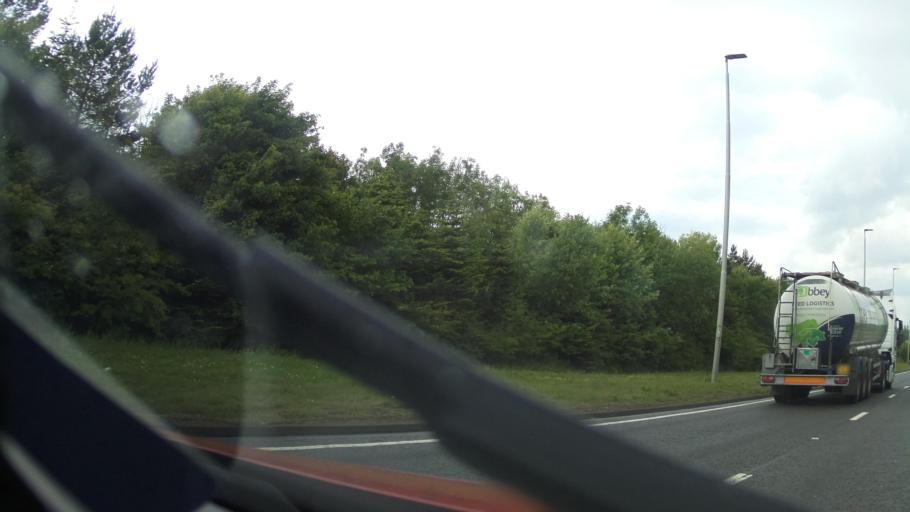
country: GB
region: England
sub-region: County Durham
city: Hawthorn
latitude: 54.8144
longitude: -1.3648
